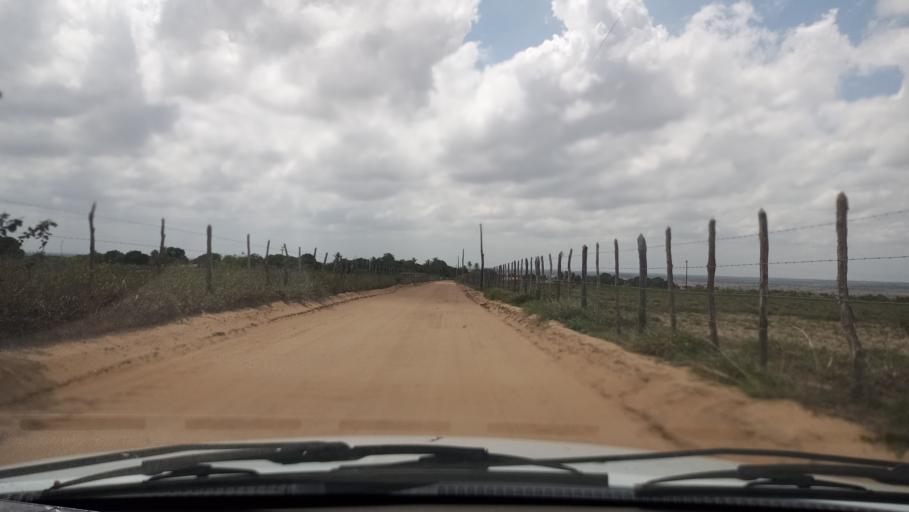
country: BR
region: Rio Grande do Norte
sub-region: Montanhas
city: Montanhas
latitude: -6.3617
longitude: -35.3330
